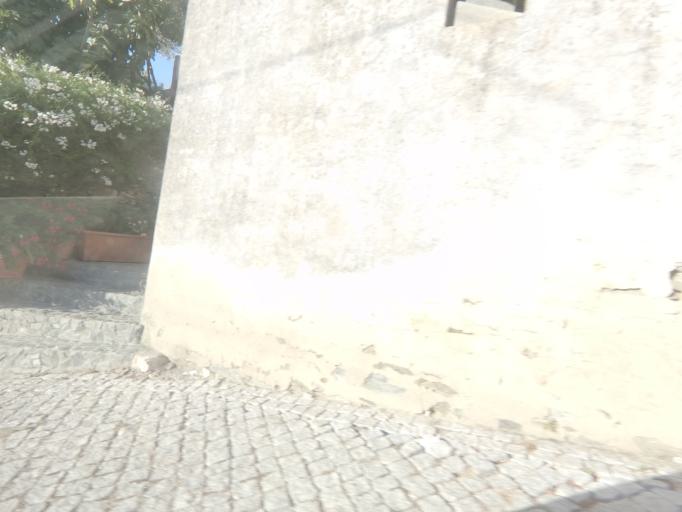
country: PT
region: Viseu
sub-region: Tabuaco
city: Tabuaco
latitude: 41.1469
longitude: -7.6071
